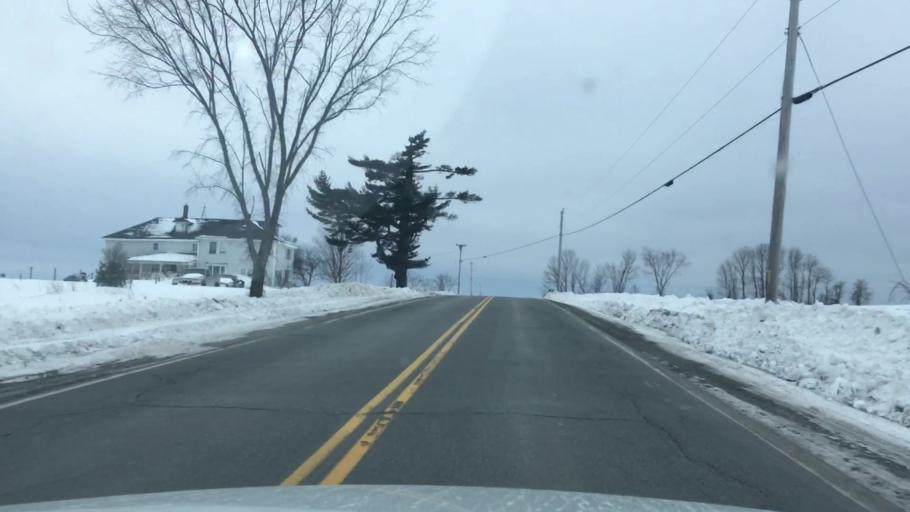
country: US
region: Maine
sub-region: Penobscot County
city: Garland
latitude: 44.9668
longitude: -69.1658
